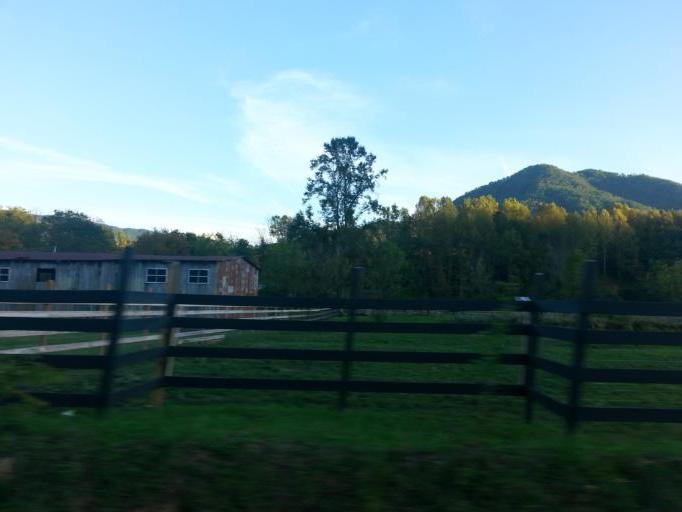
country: US
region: Tennessee
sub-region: Sevier County
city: Pigeon Forge
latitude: 35.7094
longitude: -83.6668
